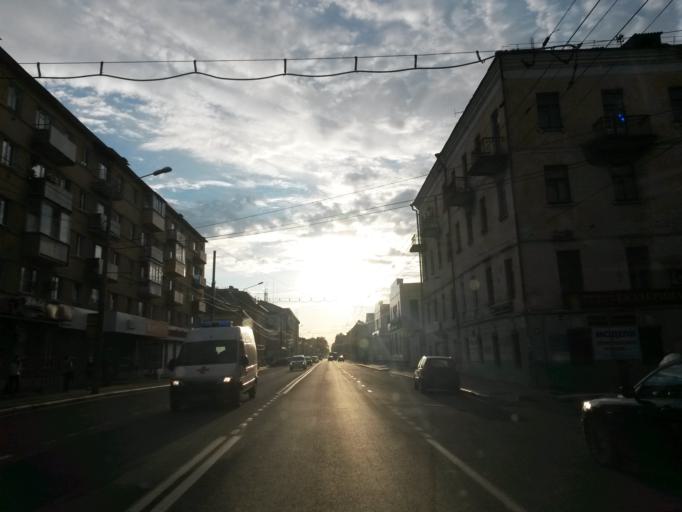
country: RU
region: Jaroslavl
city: Yaroslavl
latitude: 57.6322
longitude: 39.8854
